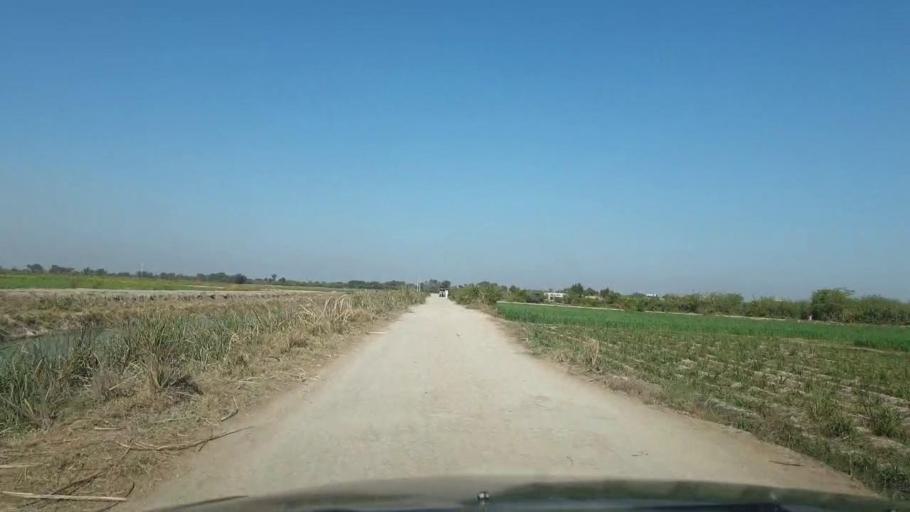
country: PK
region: Sindh
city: Mirpur Khas
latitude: 25.5684
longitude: 69.0620
